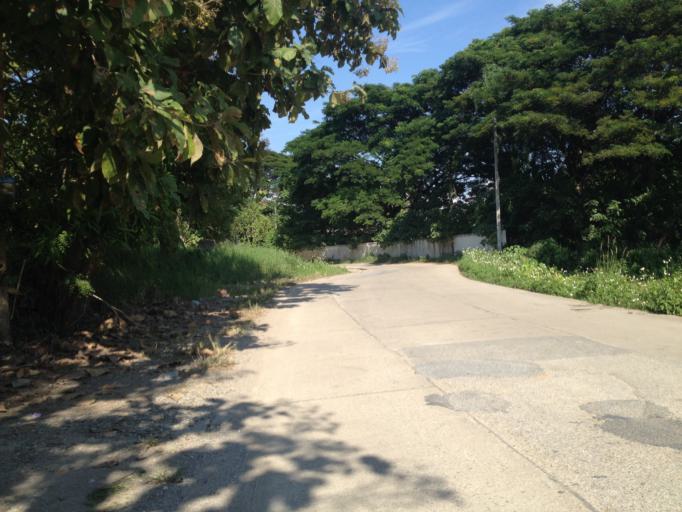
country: TH
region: Chiang Mai
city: Hang Dong
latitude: 18.7204
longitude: 98.9726
